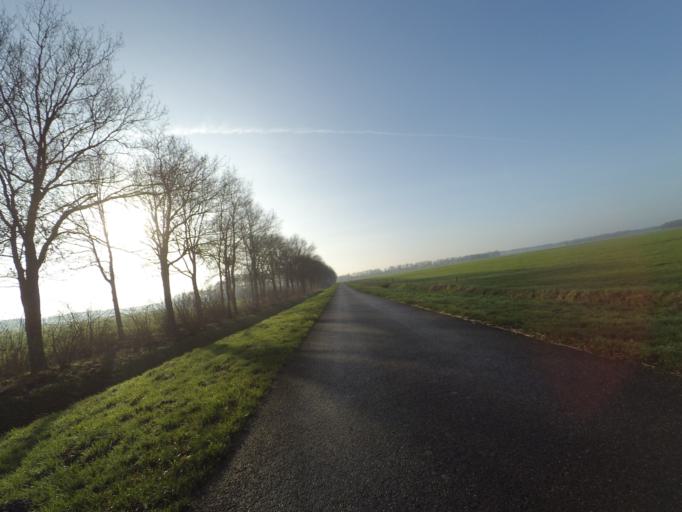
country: NL
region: Drenthe
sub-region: Gemeente Assen
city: Assen
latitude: 52.8614
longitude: 6.6463
